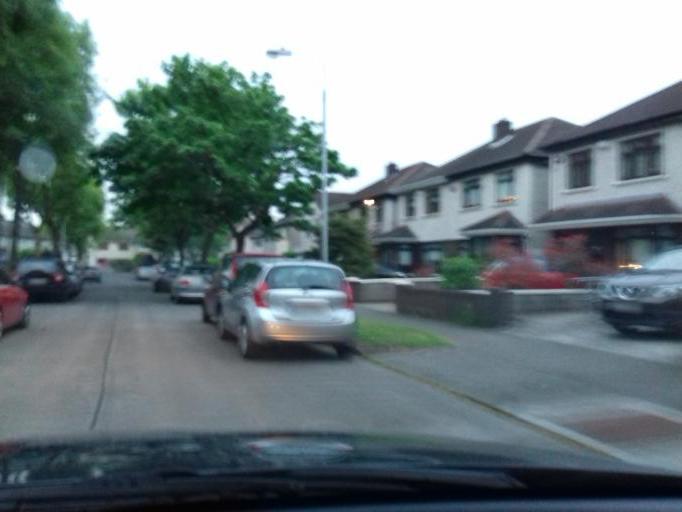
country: IE
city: Darndale
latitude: 53.3946
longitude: -6.1877
